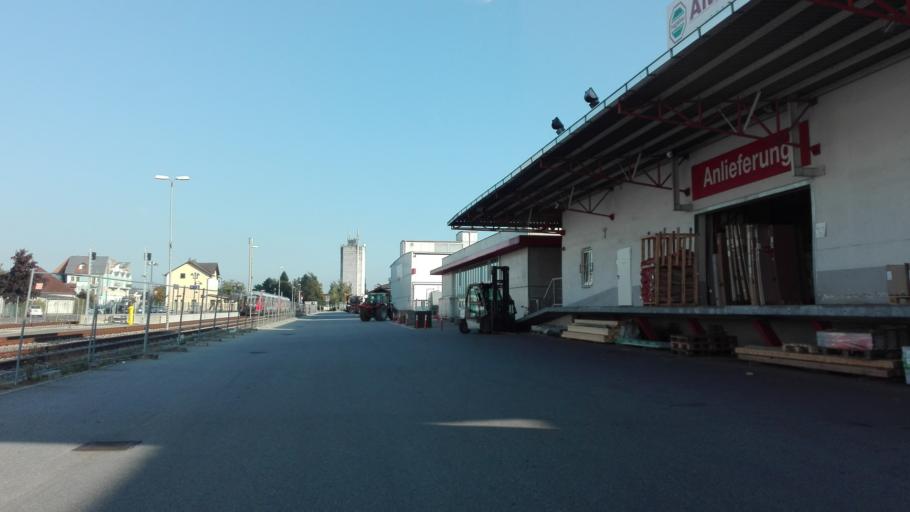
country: AT
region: Upper Austria
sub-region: Politischer Bezirk Perg
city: Perg
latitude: 48.2480
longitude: 14.6254
